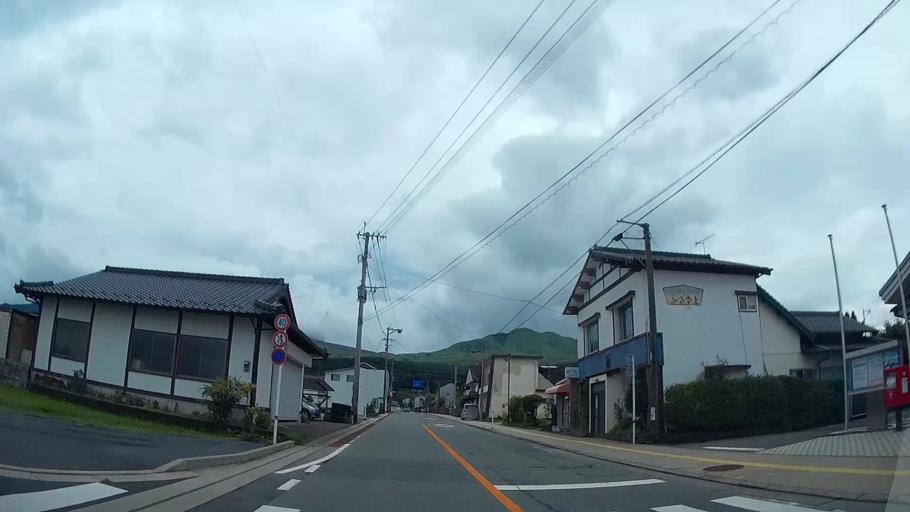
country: JP
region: Kumamoto
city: Aso
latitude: 32.9351
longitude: 131.0799
